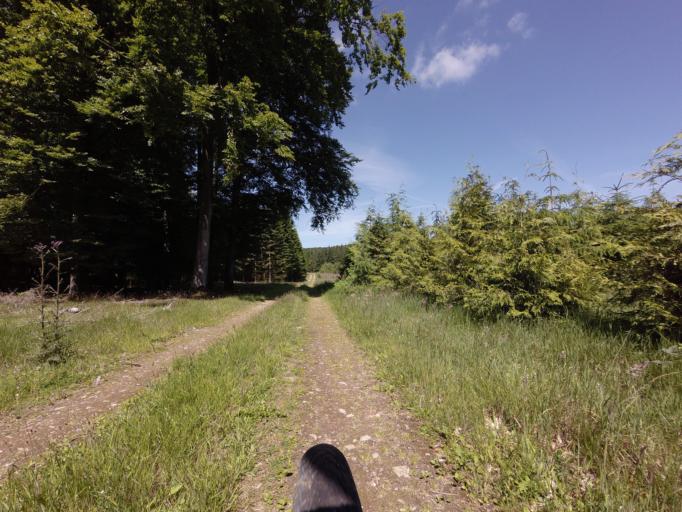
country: DK
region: Central Jutland
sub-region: Silkeborg Kommune
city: Virklund
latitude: 56.0578
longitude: 9.4766
